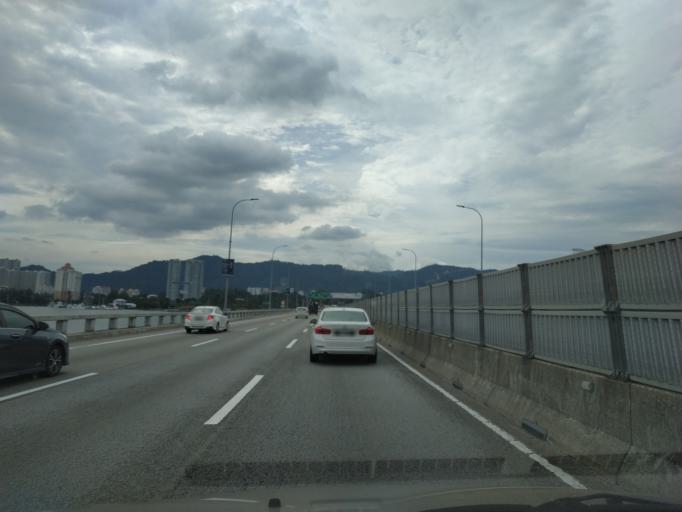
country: MY
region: Penang
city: George Town
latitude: 5.3577
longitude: 100.3222
